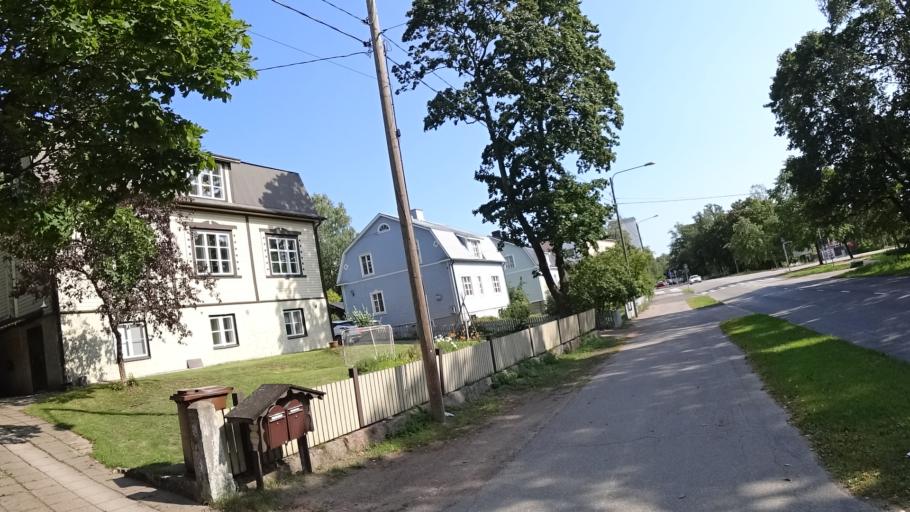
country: FI
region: Kymenlaakso
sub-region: Kotka-Hamina
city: Kotka
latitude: 60.4586
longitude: 26.9286
